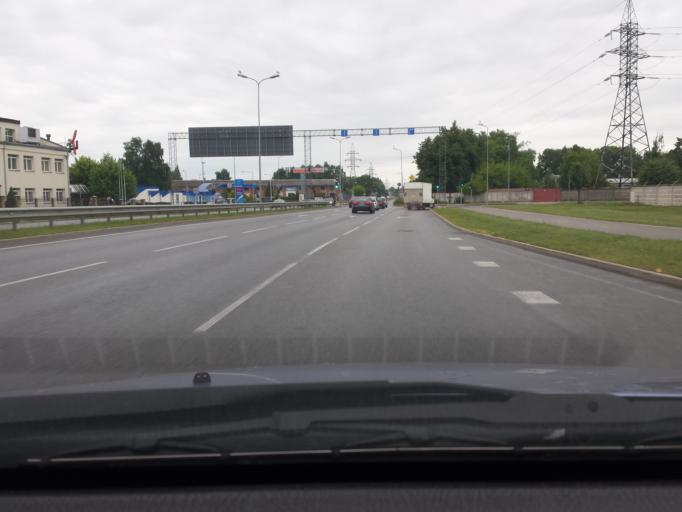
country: LV
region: Riga
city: Riga
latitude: 56.9339
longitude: 24.1778
